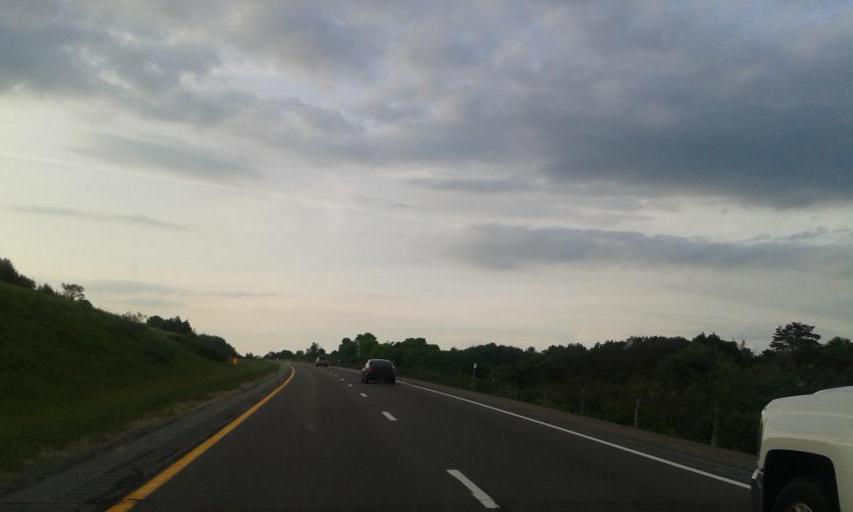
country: US
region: New York
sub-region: Broome County
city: Chenango Bridge
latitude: 42.2566
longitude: -75.9180
